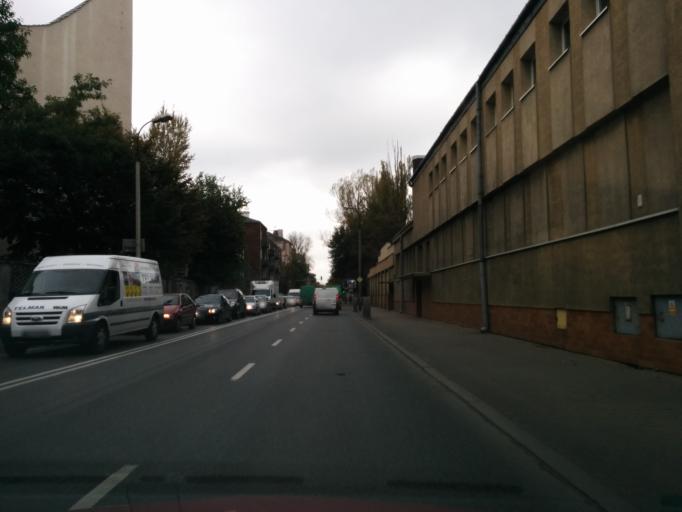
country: PL
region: Masovian Voivodeship
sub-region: Warszawa
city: Praga Polnoc
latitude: 52.2608
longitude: 21.0466
